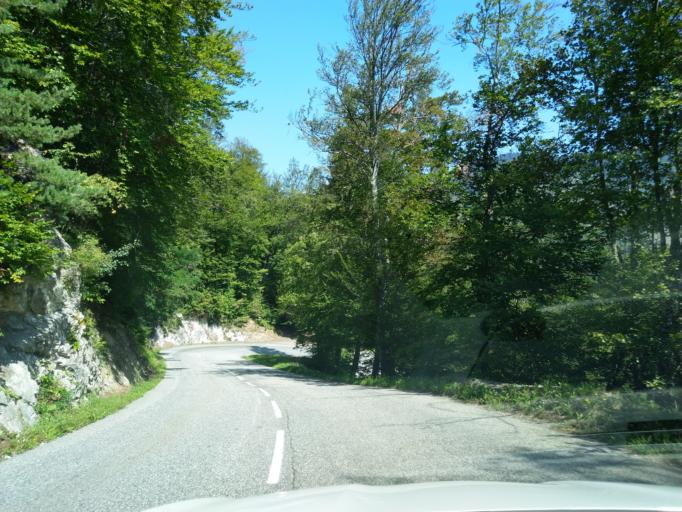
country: FR
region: Rhone-Alpes
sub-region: Departement de la Savoie
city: Les Allues
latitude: 45.4489
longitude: 6.5581
